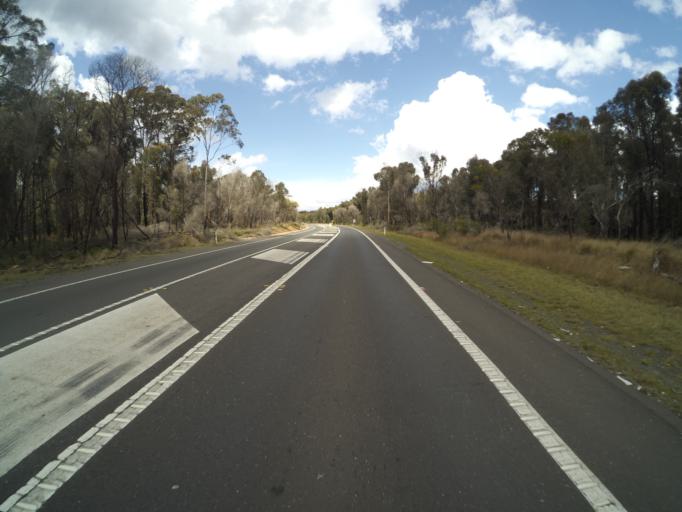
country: AU
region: New South Wales
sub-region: Wollondilly
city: Douglas Park
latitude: -34.3061
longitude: 150.7382
